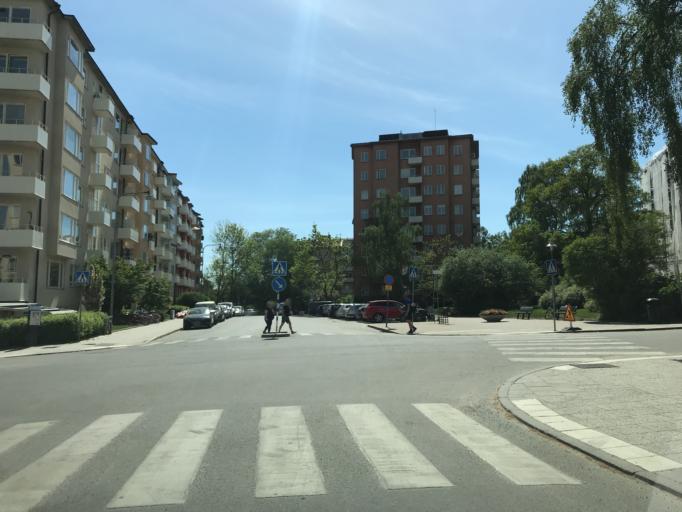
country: SE
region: Stockholm
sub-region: Stockholms Kommun
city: OEstermalm
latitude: 59.3465
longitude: 18.1003
